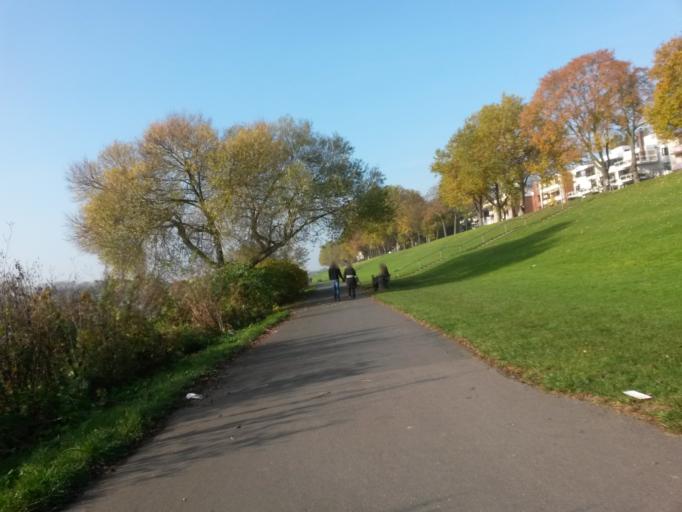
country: DE
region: Bremen
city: Bremen
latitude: 53.0683
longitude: 8.8299
